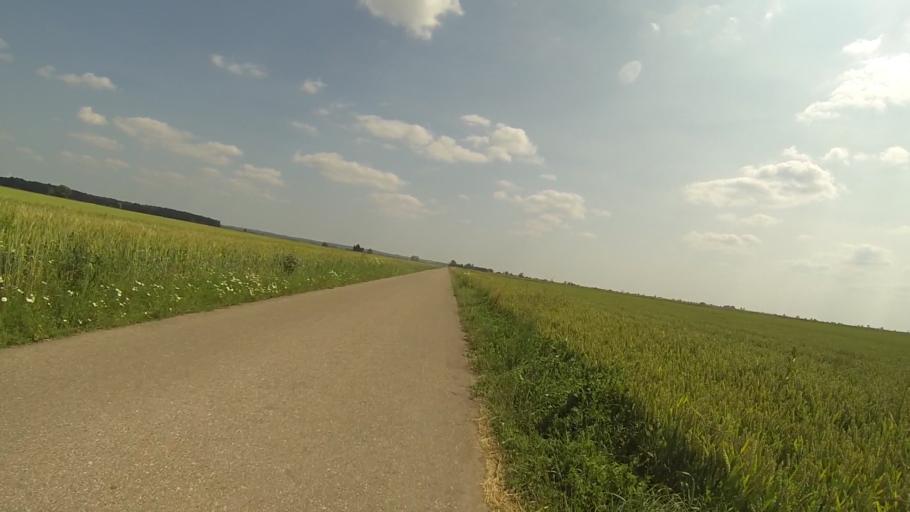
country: DE
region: Baden-Wuerttemberg
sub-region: Regierungsbezirk Stuttgart
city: Niederstotzingen
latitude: 48.5285
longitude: 10.2520
